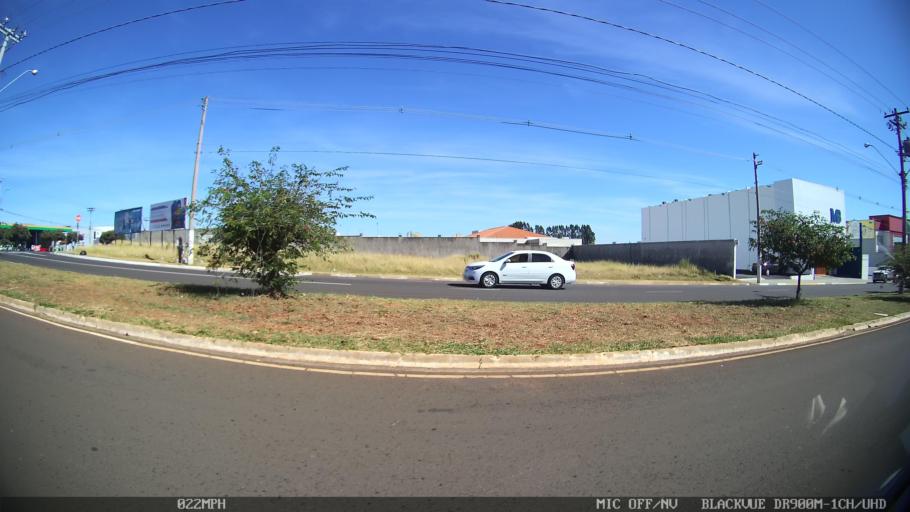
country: BR
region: Sao Paulo
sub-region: Franca
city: Franca
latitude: -20.5409
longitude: -47.3753
